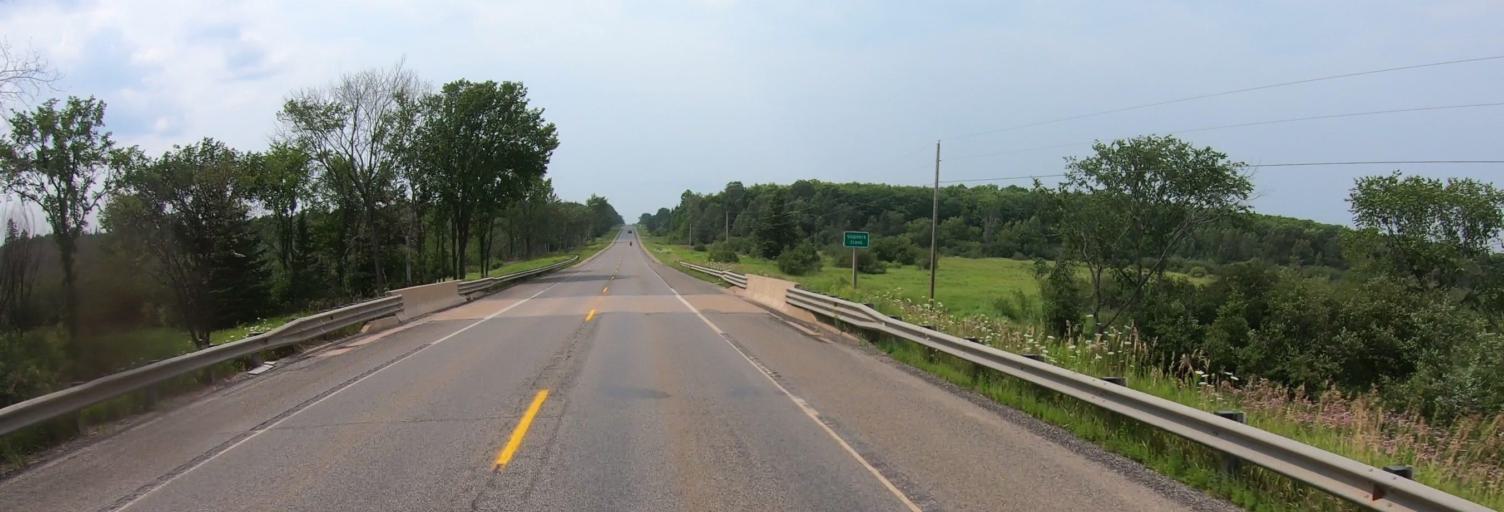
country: US
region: Michigan
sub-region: Alger County
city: Munising
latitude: 46.3330
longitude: -86.8787
